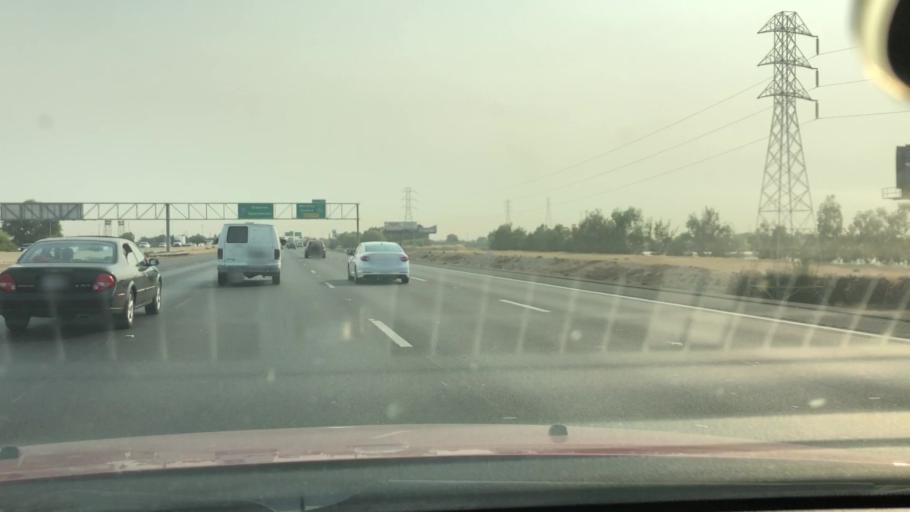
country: US
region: California
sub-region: San Joaquin County
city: Lathrop
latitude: 37.7765
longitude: -121.3183
